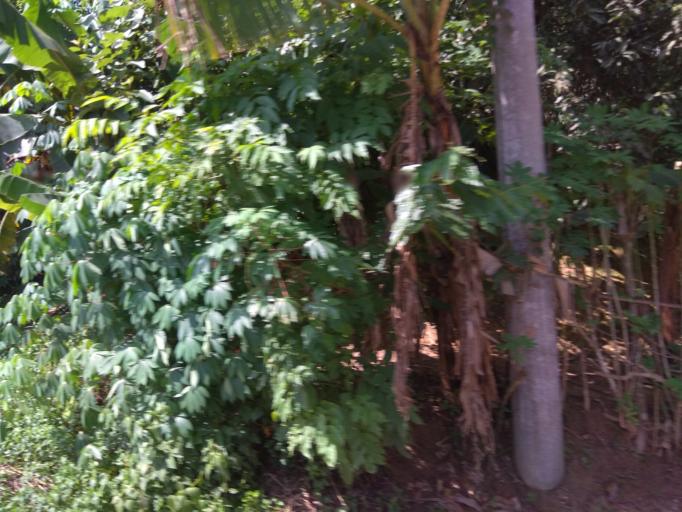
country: BD
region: Chittagong
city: Khagrachhari
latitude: 23.0365
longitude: 92.0052
